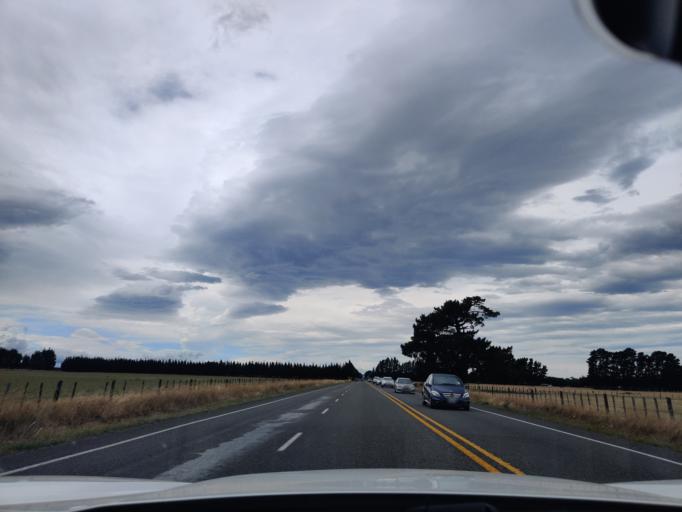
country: NZ
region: Wellington
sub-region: Masterton District
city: Masterton
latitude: -40.9947
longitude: 175.5645
